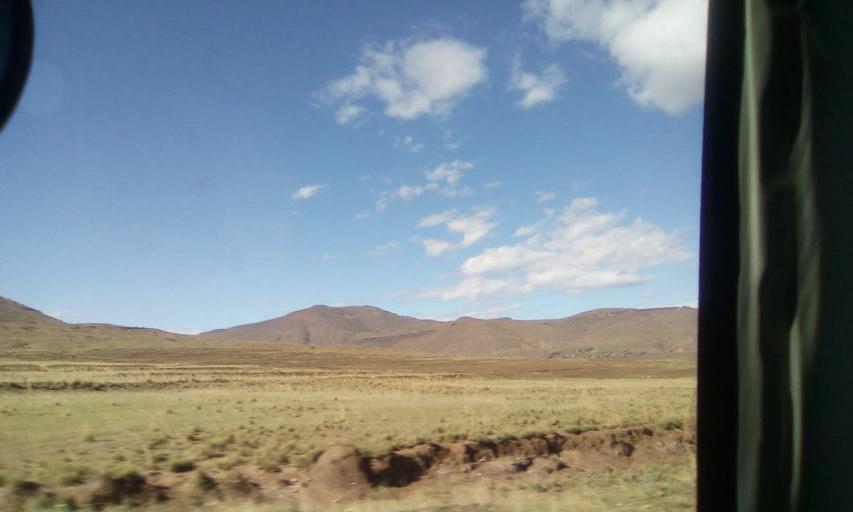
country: LS
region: Qacha's Nek
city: Qacha's Nek
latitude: -30.0387
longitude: 28.2633
